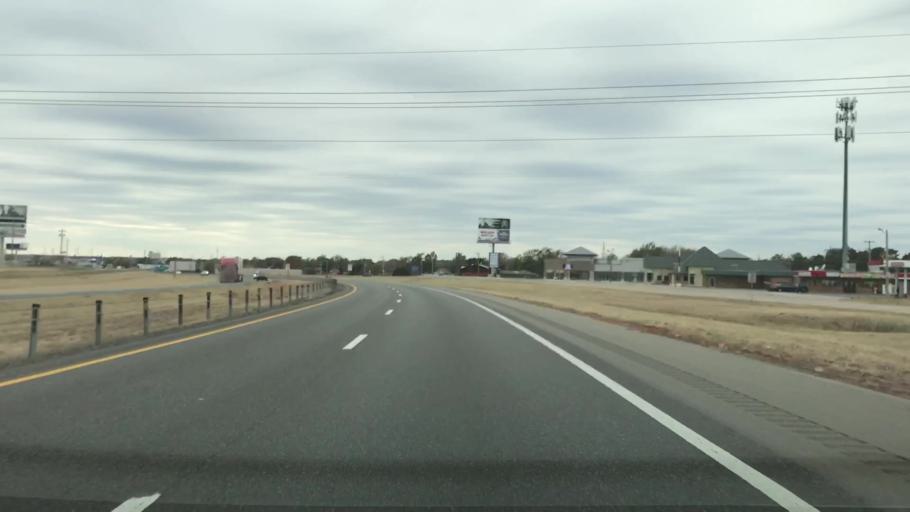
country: US
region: Oklahoma
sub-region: Custer County
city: Weatherford
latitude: 35.5364
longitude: -98.6762
